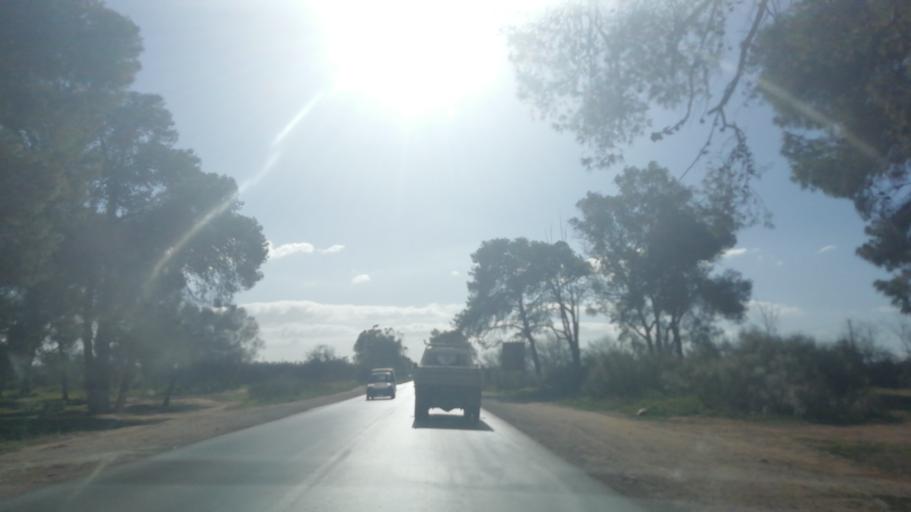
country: DZ
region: Mostaganem
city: Mostaganem
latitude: 35.9763
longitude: 0.2740
